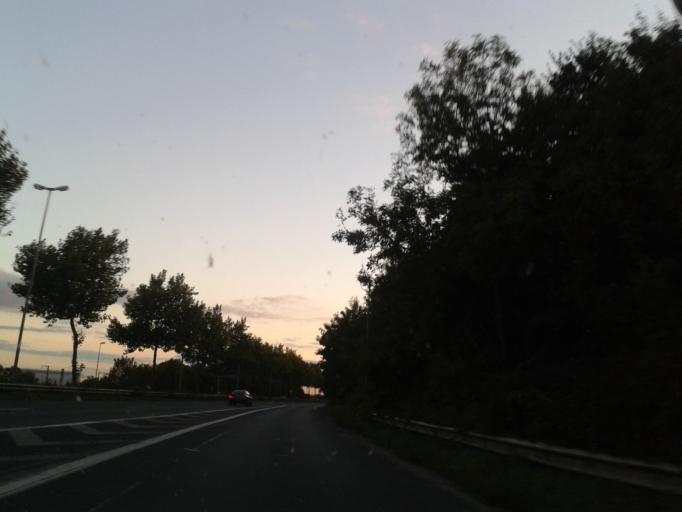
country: DE
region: North Rhine-Westphalia
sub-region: Regierungsbezirk Detmold
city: Bielefeld
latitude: 51.9985
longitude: 8.4981
